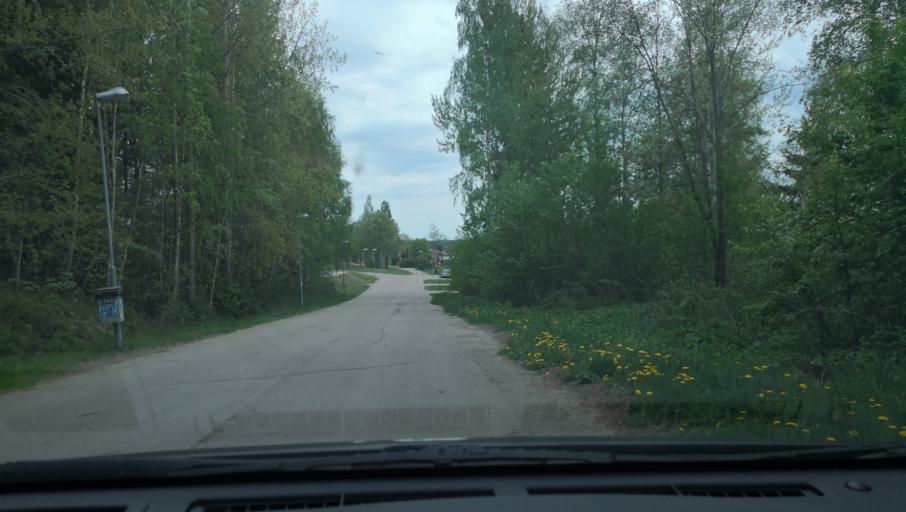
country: SE
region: Vaestmanland
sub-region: Skinnskattebergs Kommun
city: Skinnskatteberg
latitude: 59.8297
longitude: 15.6962
